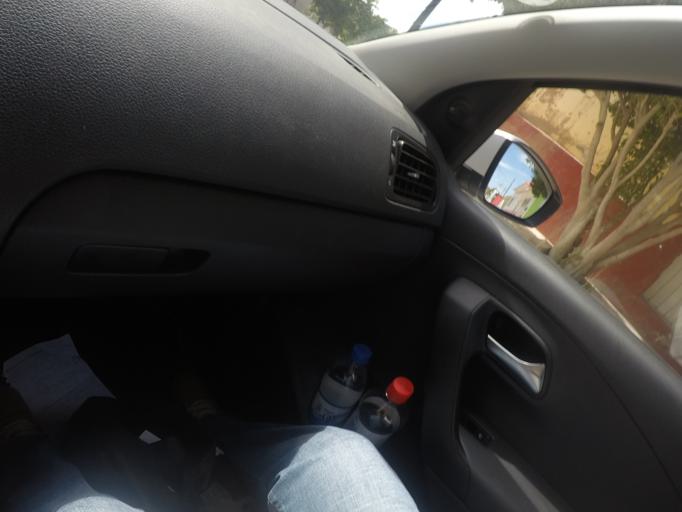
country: MX
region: Oaxaca
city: San Blas Atempa
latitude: 16.3357
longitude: -95.2301
